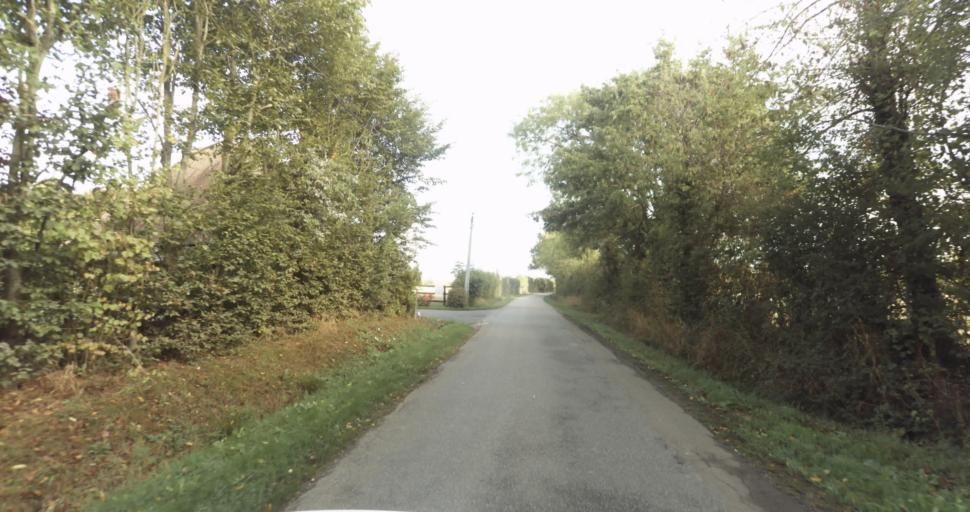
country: FR
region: Lower Normandy
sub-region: Departement de l'Orne
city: Gace
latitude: 48.8753
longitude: 0.3323
